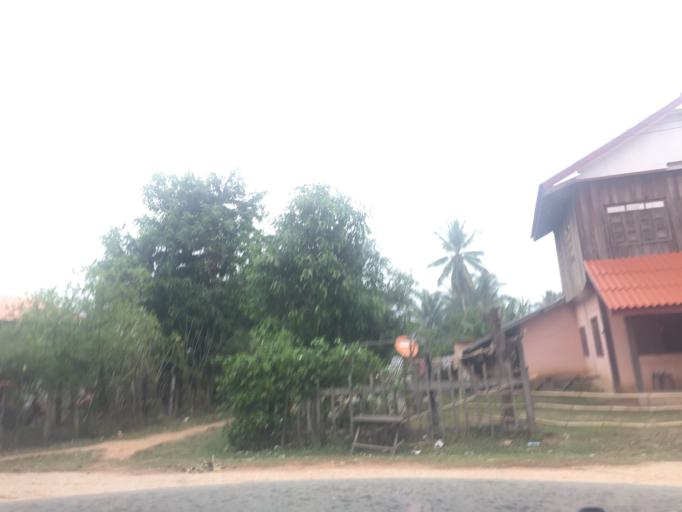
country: LA
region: Xiagnabouli
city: Sainyabuli
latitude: 19.0357
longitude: 101.5254
